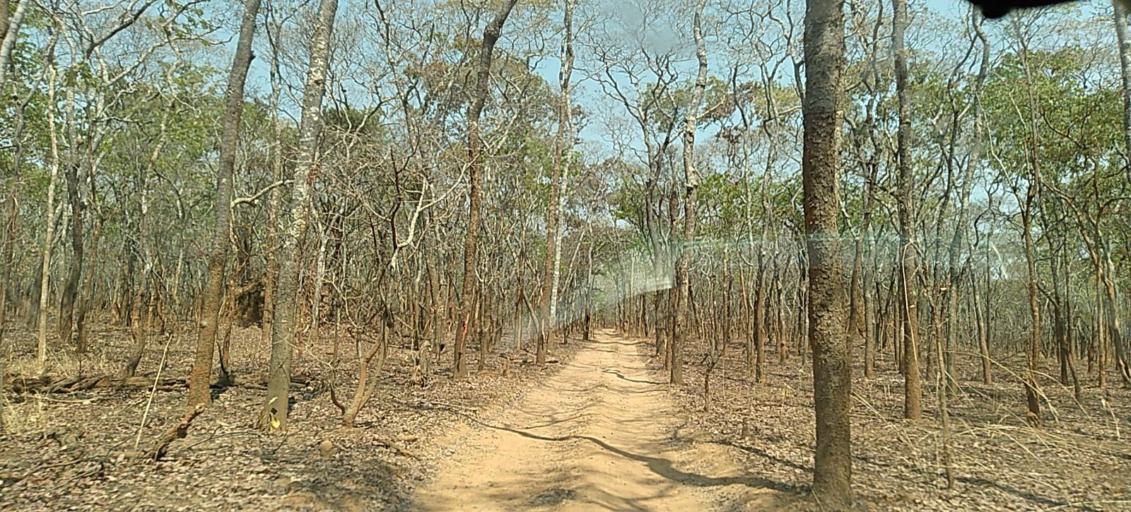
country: ZM
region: North-Western
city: Kasempa
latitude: -13.3933
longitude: 25.6009
